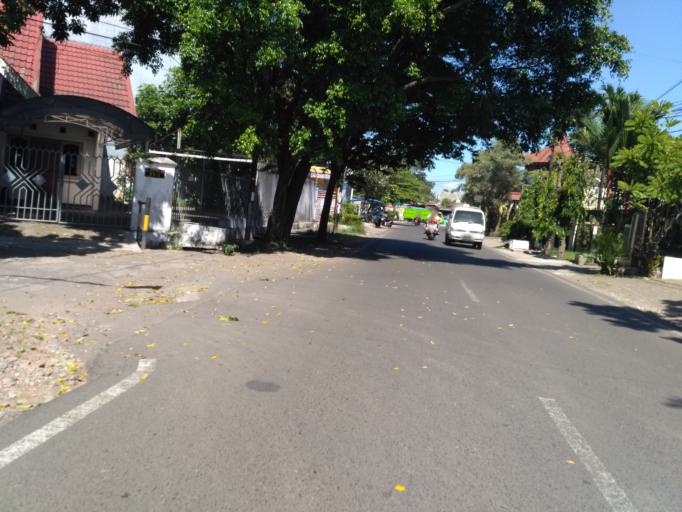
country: ID
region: East Java
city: Malang
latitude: -7.9800
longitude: 112.6629
